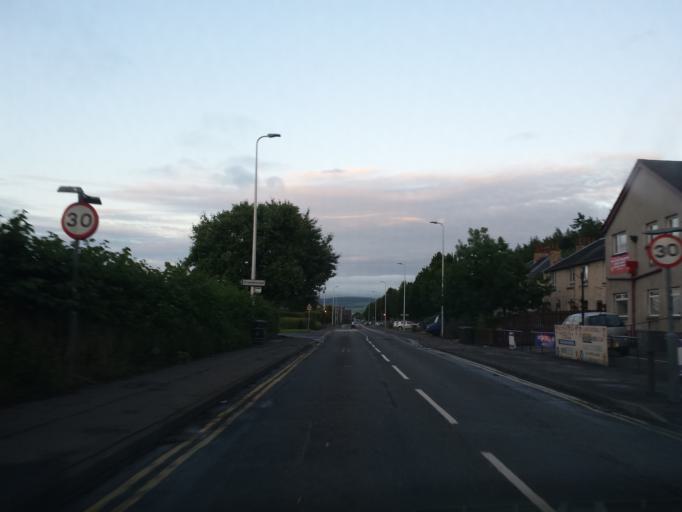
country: GB
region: Scotland
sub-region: Perth and Kinross
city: Perth
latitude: 56.4075
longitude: -3.4719
